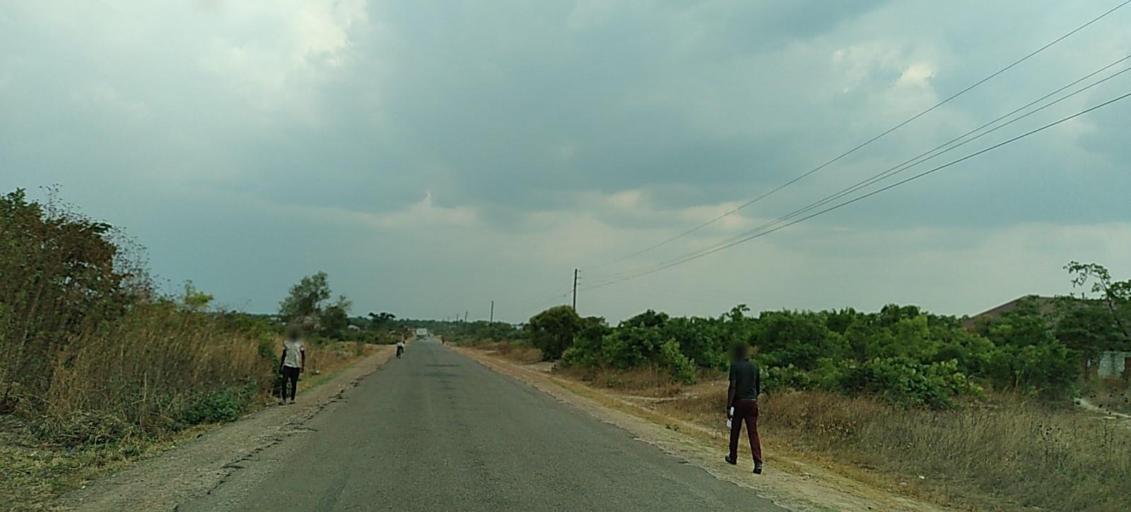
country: ZM
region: Copperbelt
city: Kalulushi
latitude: -12.8628
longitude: 28.1215
